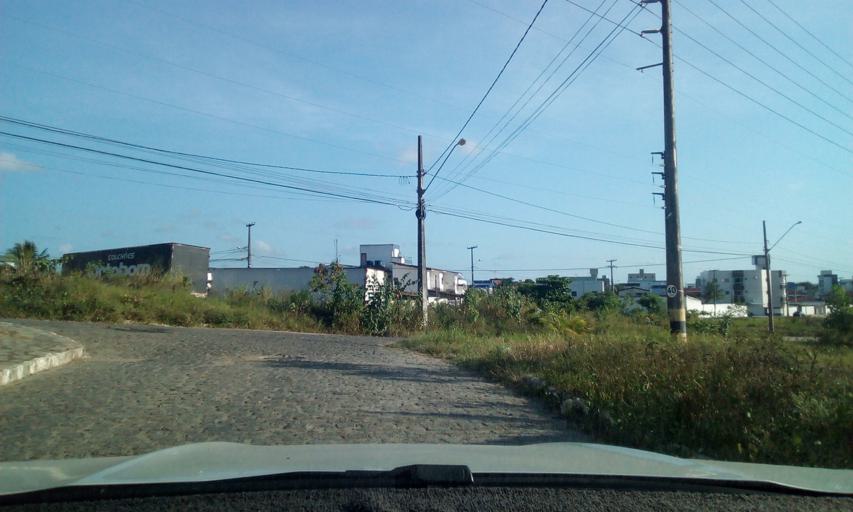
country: BR
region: Paraiba
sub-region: Joao Pessoa
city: Joao Pessoa
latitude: -7.1703
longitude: -34.8852
